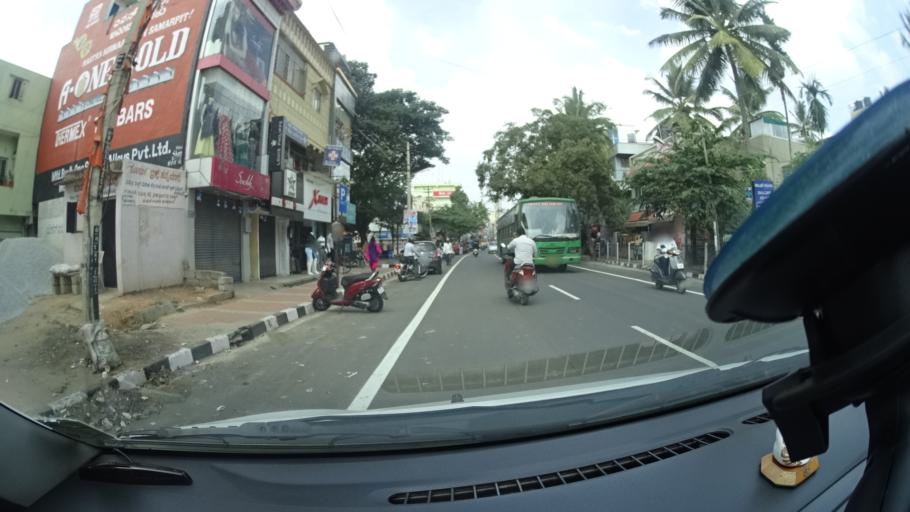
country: IN
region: Karnataka
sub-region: Bangalore Urban
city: Yelahanka
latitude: 13.0938
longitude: 77.5819
